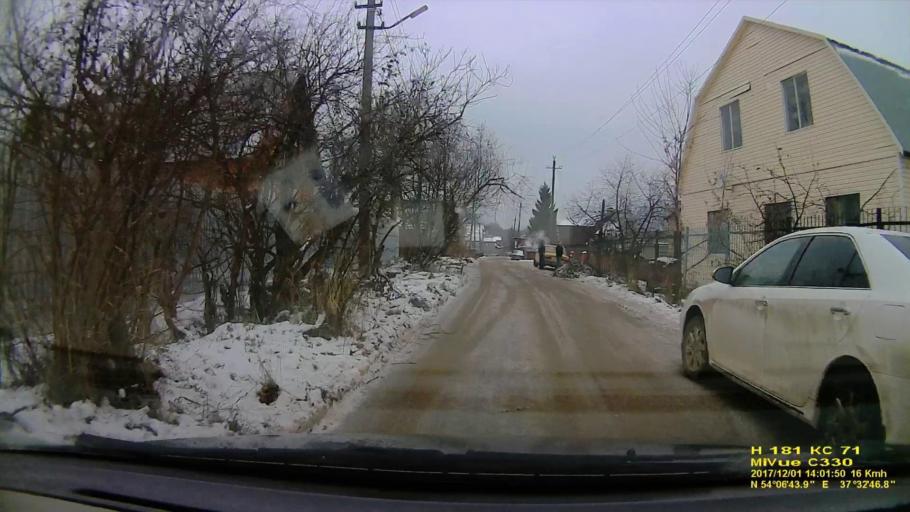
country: RU
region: Tula
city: Kosaya Gora
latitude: 54.1122
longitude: 37.5463
